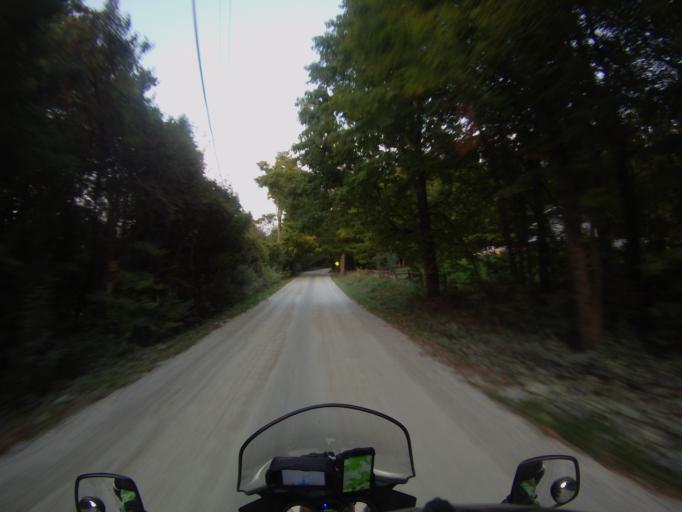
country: US
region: Vermont
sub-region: Rutland County
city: Brandon
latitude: 43.7831
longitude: -73.1386
